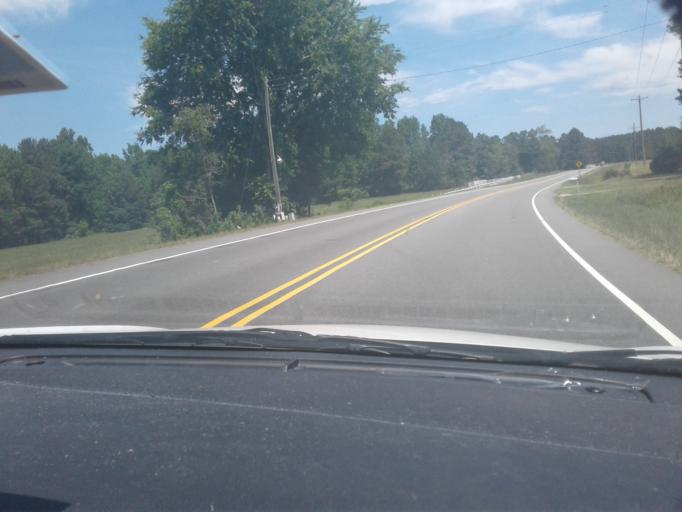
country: US
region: North Carolina
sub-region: Harnett County
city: Lillington
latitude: 35.4364
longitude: -78.8287
